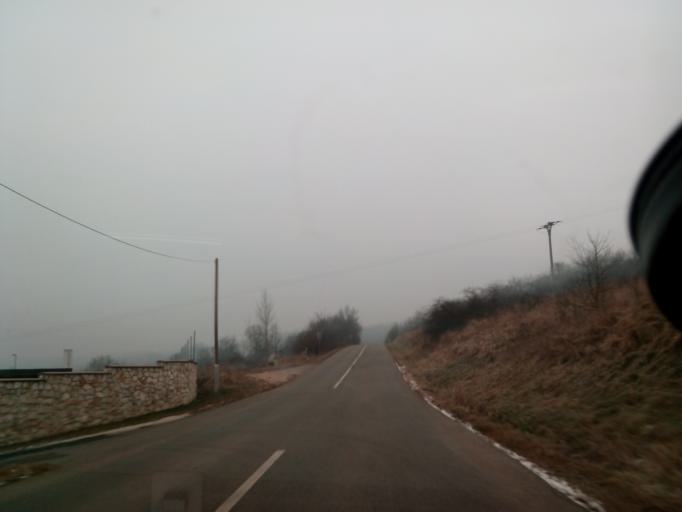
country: SK
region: Kosicky
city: Kosice
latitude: 48.7069
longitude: 21.1545
